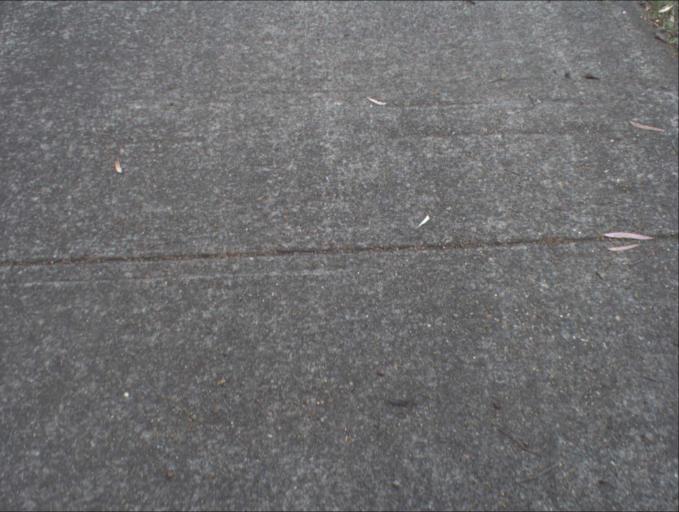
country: AU
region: Queensland
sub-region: Logan
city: Park Ridge South
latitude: -27.6735
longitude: 153.0319
